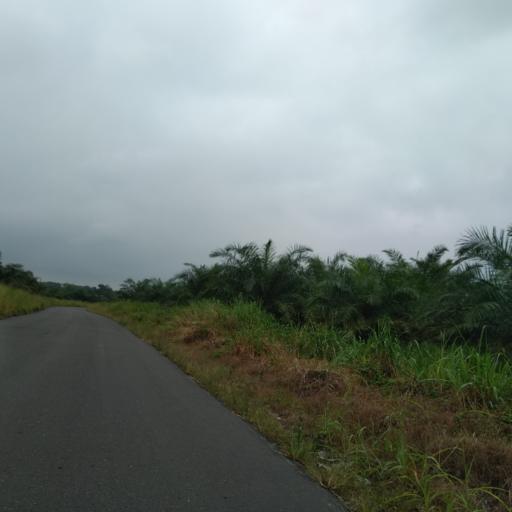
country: EC
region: Los Rios
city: Quevedo
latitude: -0.9700
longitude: -79.3523
